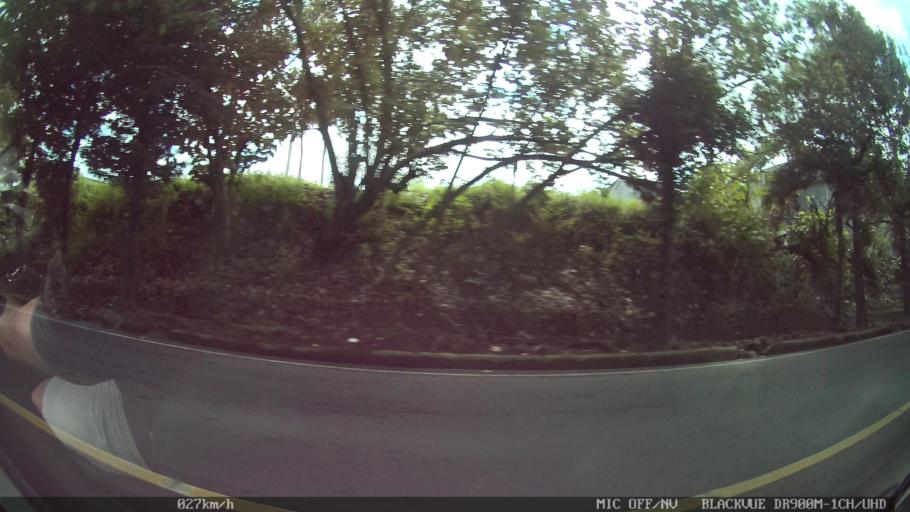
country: ID
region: Bali
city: Banjar Sedang
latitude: -8.5662
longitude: 115.2942
